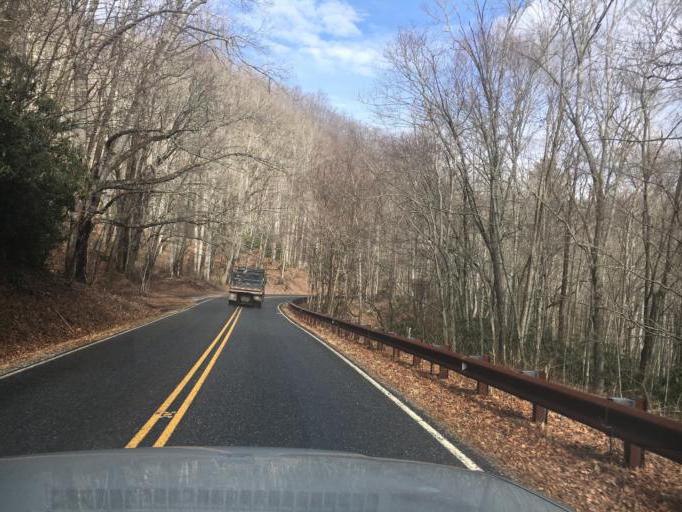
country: US
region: North Carolina
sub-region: Transylvania County
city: Brevard
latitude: 35.3713
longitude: -82.8160
